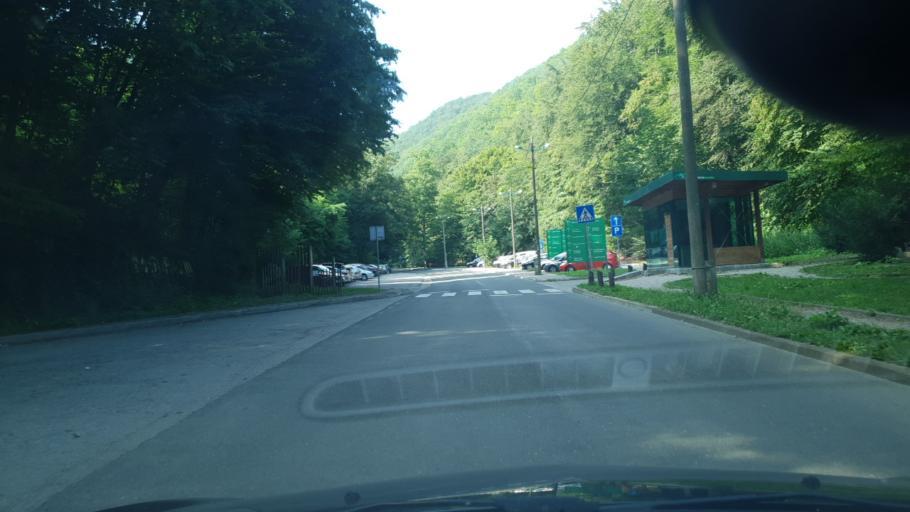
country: HR
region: Grad Zagreb
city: Kasina
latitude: 45.8690
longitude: 15.9786
